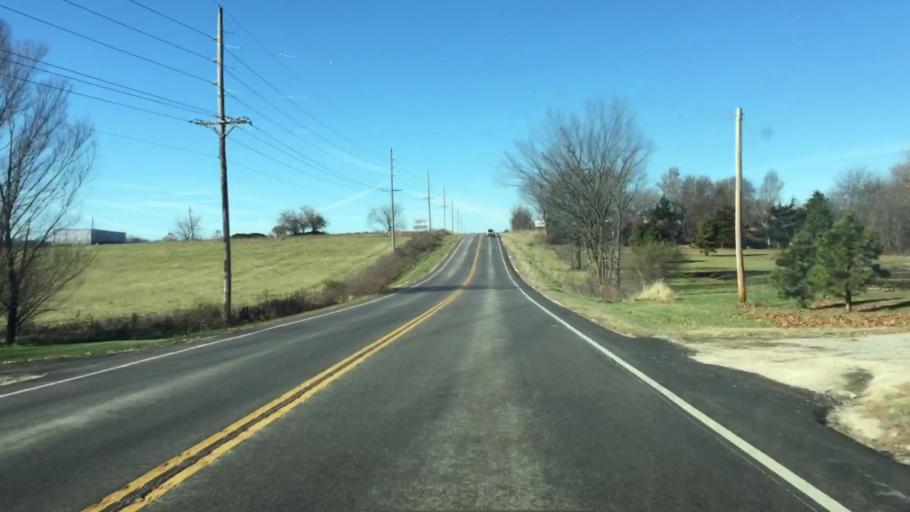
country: US
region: Missouri
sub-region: Miller County
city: Eldon
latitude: 38.3738
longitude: -92.6267
